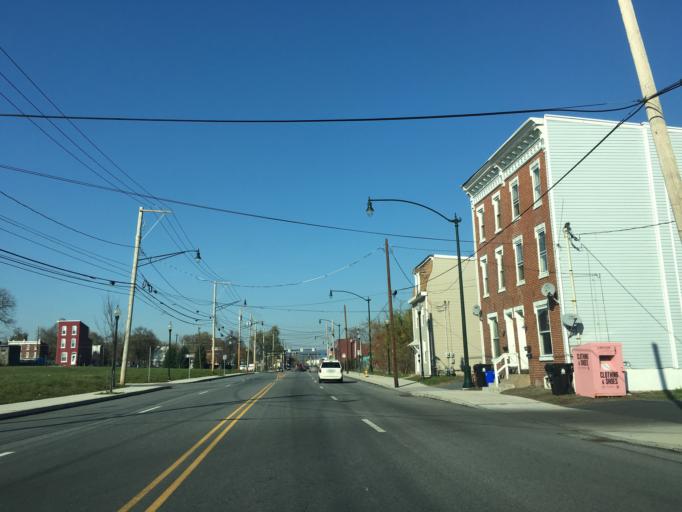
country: US
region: Pennsylvania
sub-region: Dauphin County
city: Harrisburg
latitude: 40.2791
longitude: -76.8876
